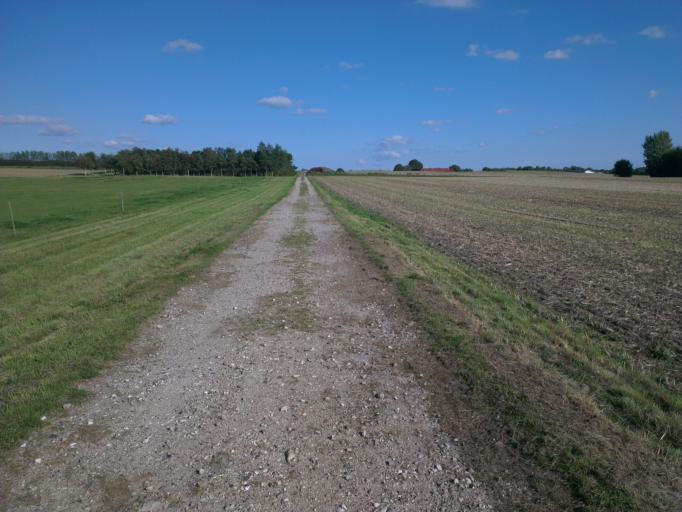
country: DK
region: Capital Region
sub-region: Frederikssund Kommune
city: Jaegerspris
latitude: 55.8397
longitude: 11.9719
